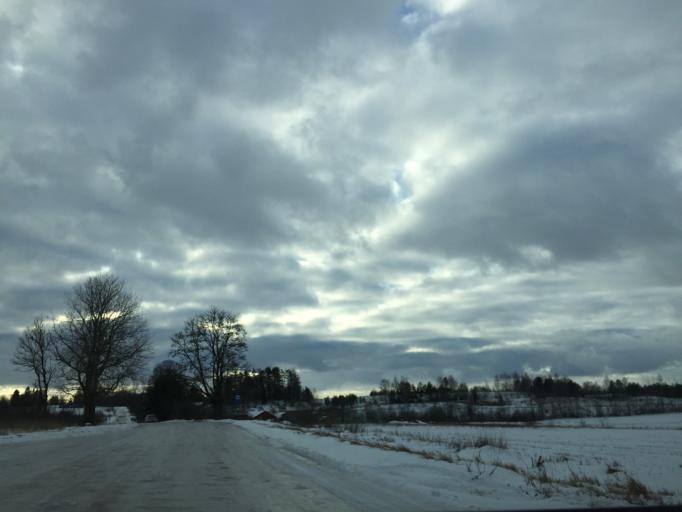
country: LV
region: Lielvarde
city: Lielvarde
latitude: 56.5842
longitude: 24.7343
